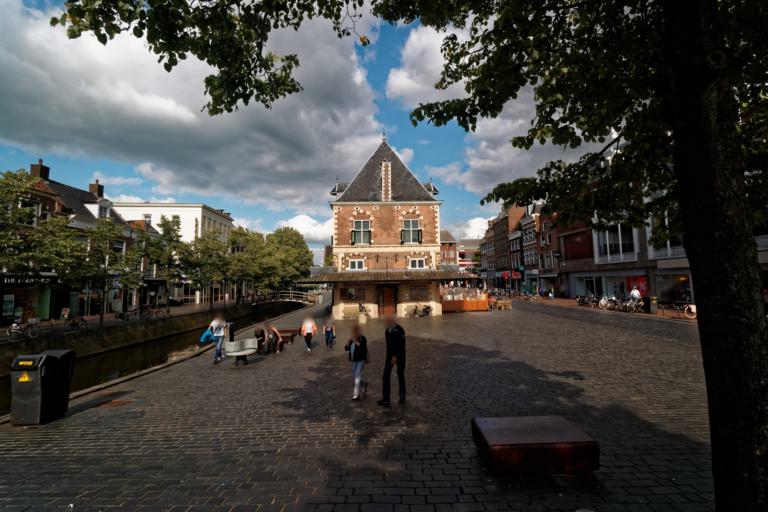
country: NL
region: Friesland
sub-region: Gemeente Leeuwarden
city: Leeuwarden
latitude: 53.2007
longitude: 5.7954
